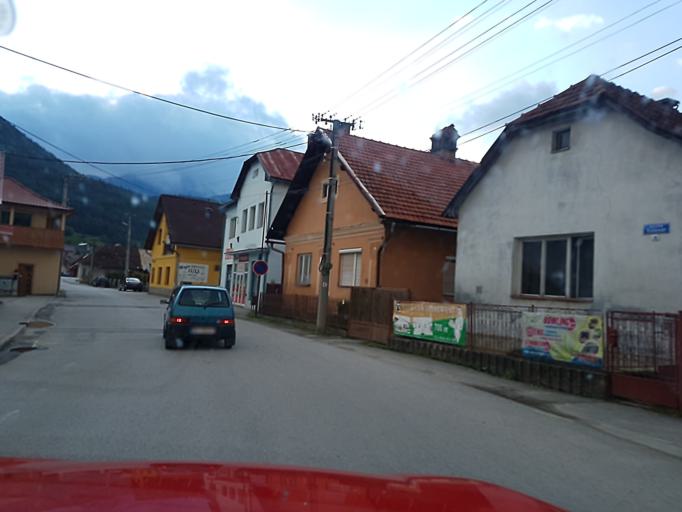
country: SK
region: Zilinsky
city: Ruzomberok
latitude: 49.1270
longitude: 19.4050
